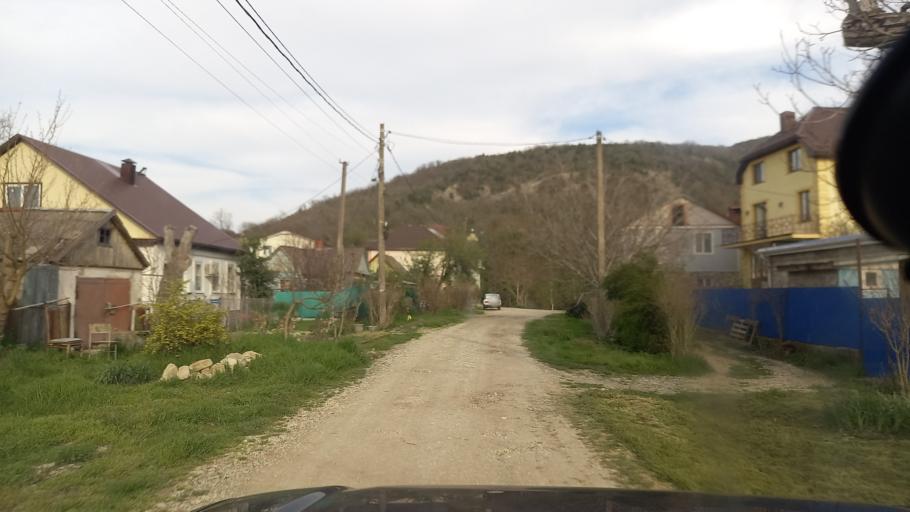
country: RU
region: Krasnodarskiy
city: Arkhipo-Osipovka
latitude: 44.3656
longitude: 38.5434
